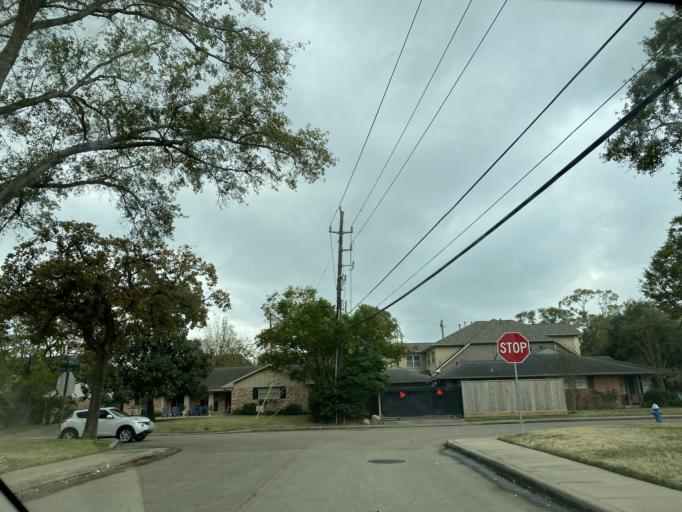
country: US
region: Texas
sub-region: Harris County
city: Hunters Creek Village
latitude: 29.7414
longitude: -95.4924
